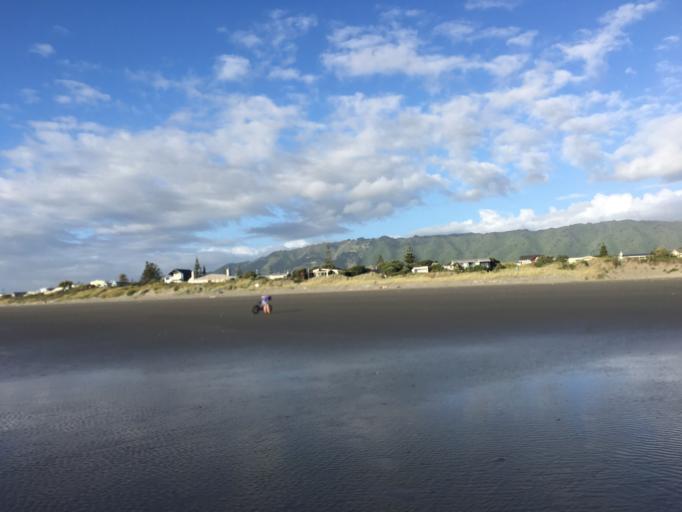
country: NZ
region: Wellington
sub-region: Kapiti Coast District
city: Paraparaumu
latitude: -40.8565
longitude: 175.0282
